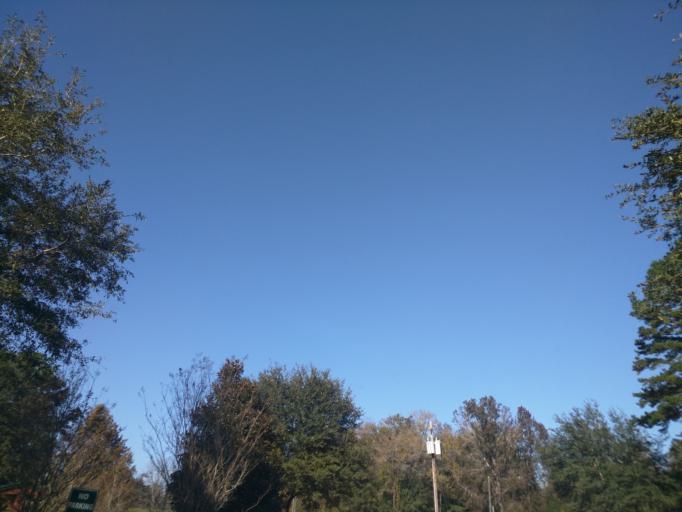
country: US
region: Florida
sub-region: Leon County
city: Tallahassee
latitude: 30.4419
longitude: -84.2130
